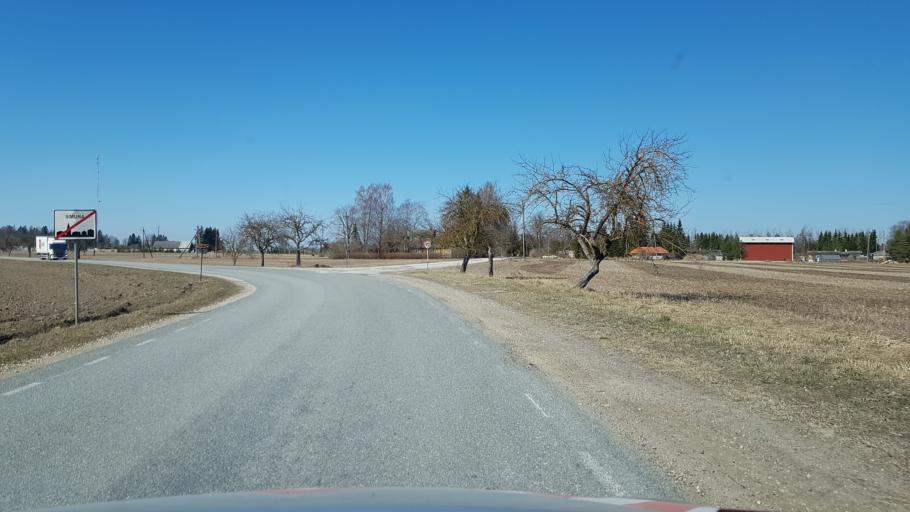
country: EE
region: Laeaene-Virumaa
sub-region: Rakke vald
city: Rakke
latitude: 59.0484
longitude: 26.3923
